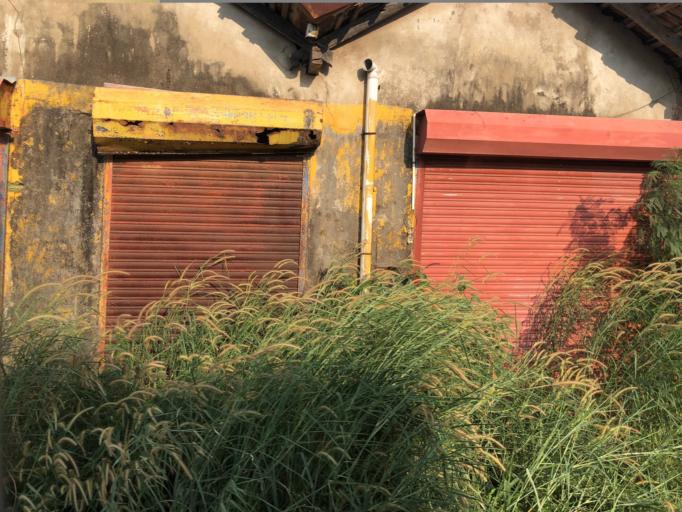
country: IN
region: Karnataka
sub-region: Dakshina Kannada
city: Ullal
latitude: 12.8598
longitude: 74.8329
